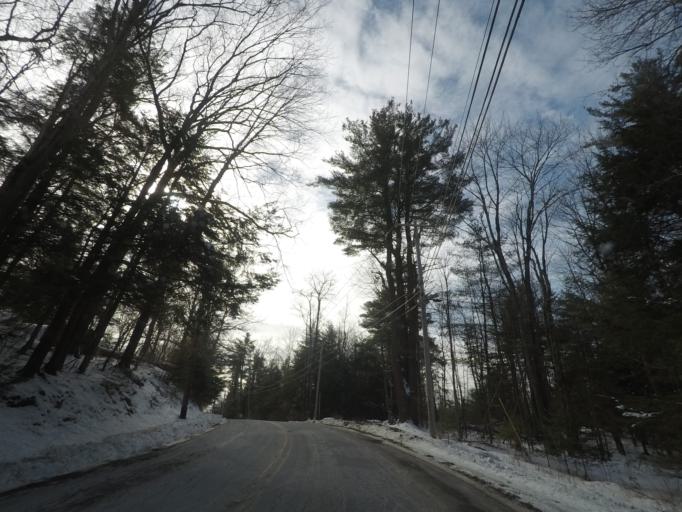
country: US
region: New York
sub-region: Rensselaer County
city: Averill Park
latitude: 42.5796
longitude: -73.4906
